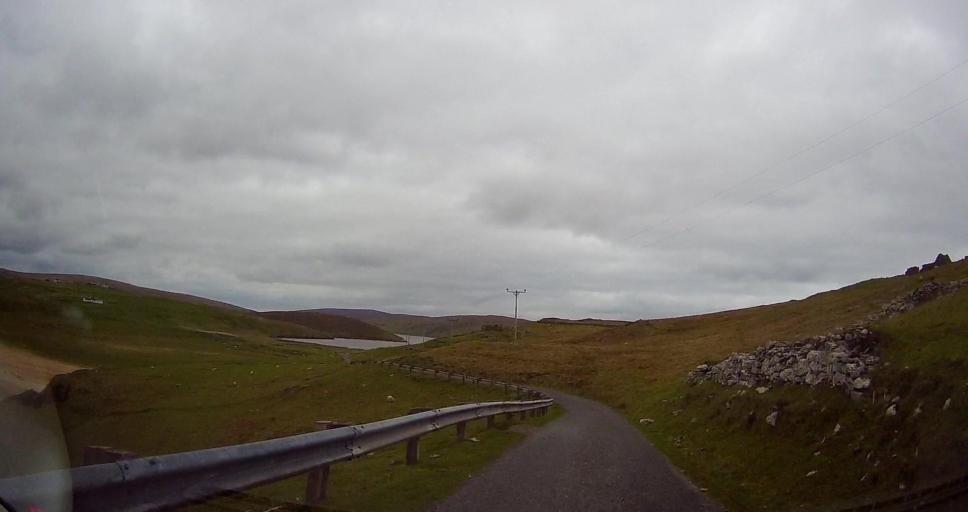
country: GB
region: Scotland
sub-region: Shetland Islands
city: Shetland
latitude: 60.8083
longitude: -0.8796
